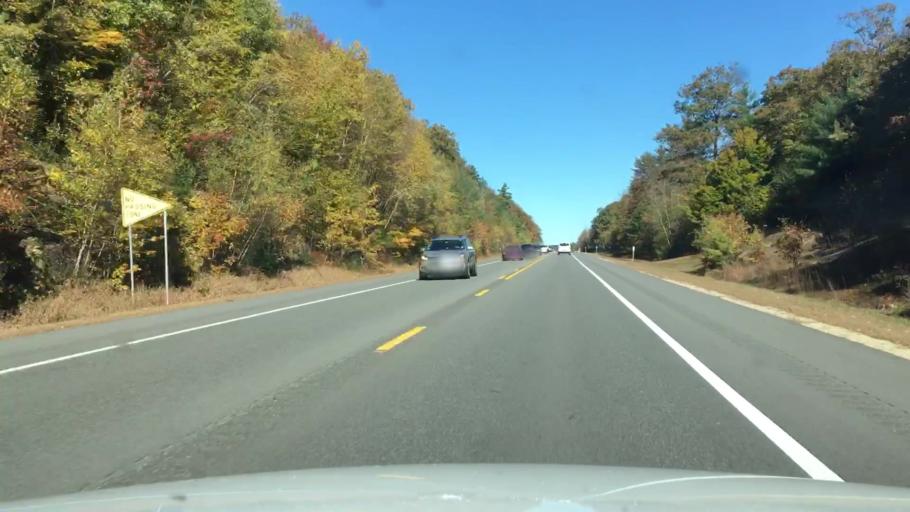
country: US
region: New Hampshire
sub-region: Strafford County
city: Rochester
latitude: 43.3618
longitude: -70.9871
